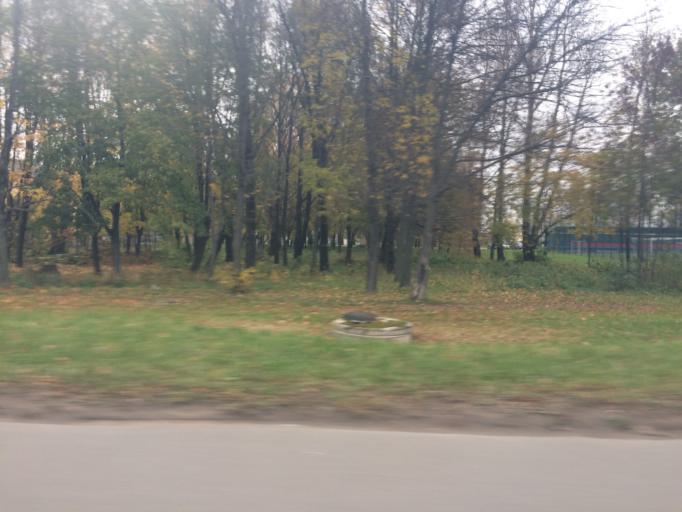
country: RU
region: Leningrad
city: Rybatskoye
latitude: 59.8500
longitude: 30.4824
